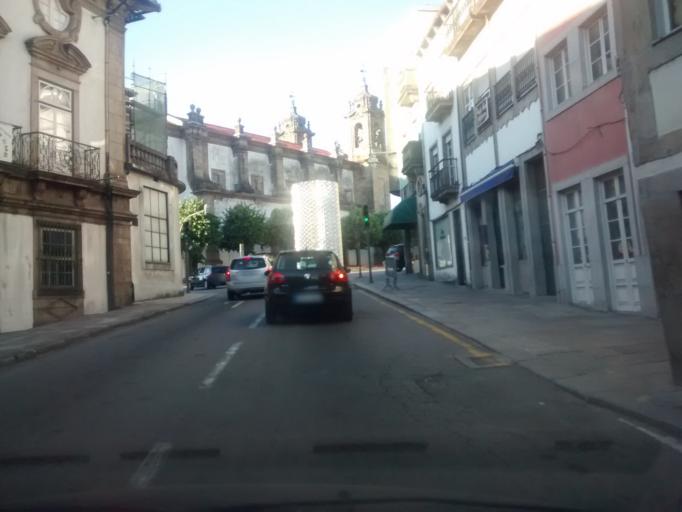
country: PT
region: Braga
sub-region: Braga
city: Braga
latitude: 41.5512
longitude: -8.4293
